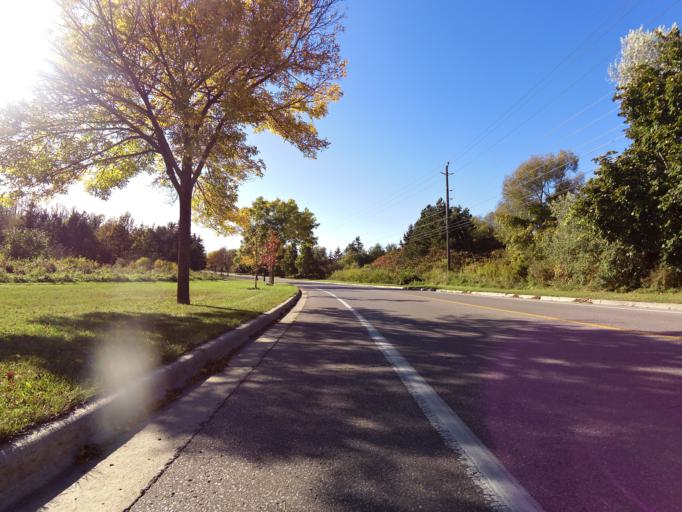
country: CA
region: Ontario
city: Oshawa
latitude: 43.8827
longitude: -78.8119
